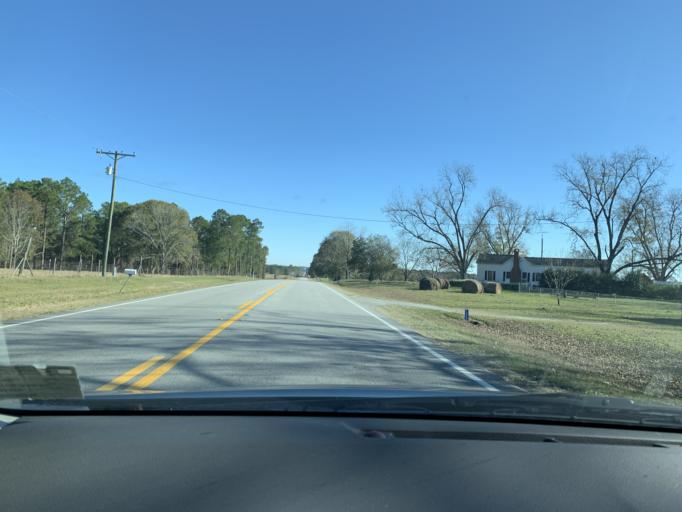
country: US
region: Georgia
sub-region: Ben Hill County
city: Fitzgerald
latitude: 31.7429
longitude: -83.1509
